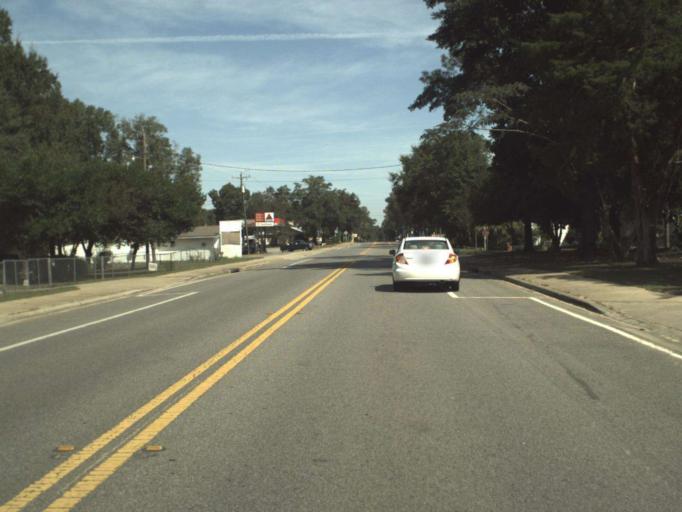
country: US
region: Florida
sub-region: Washington County
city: Chipley
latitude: 30.6291
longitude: -85.5905
